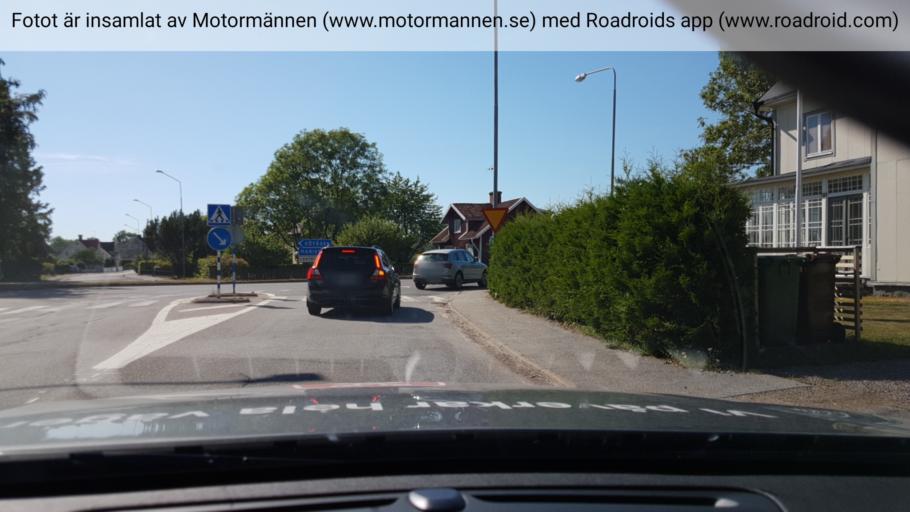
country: SE
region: Vaestra Goetaland
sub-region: Toreboda Kommun
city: Toereboda
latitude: 58.7108
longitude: 14.1363
